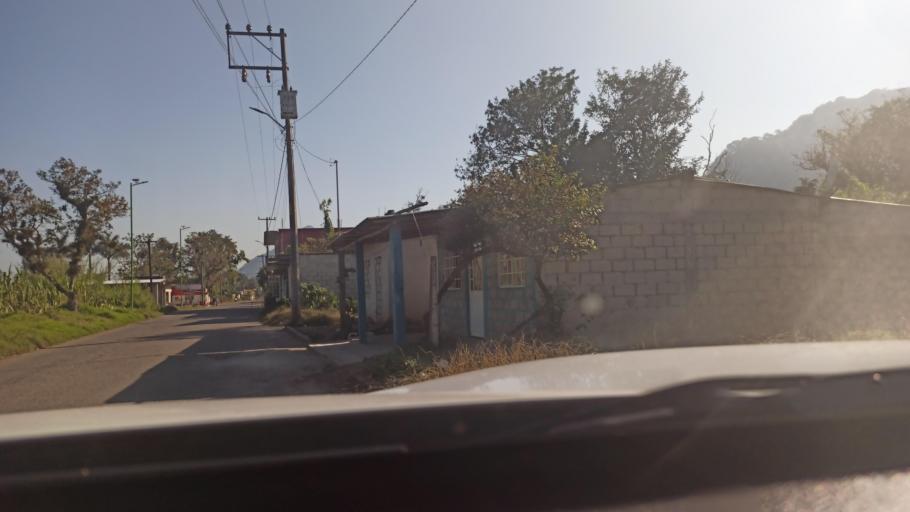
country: MX
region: Veracruz
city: Atzacan
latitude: 18.9130
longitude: -97.0859
